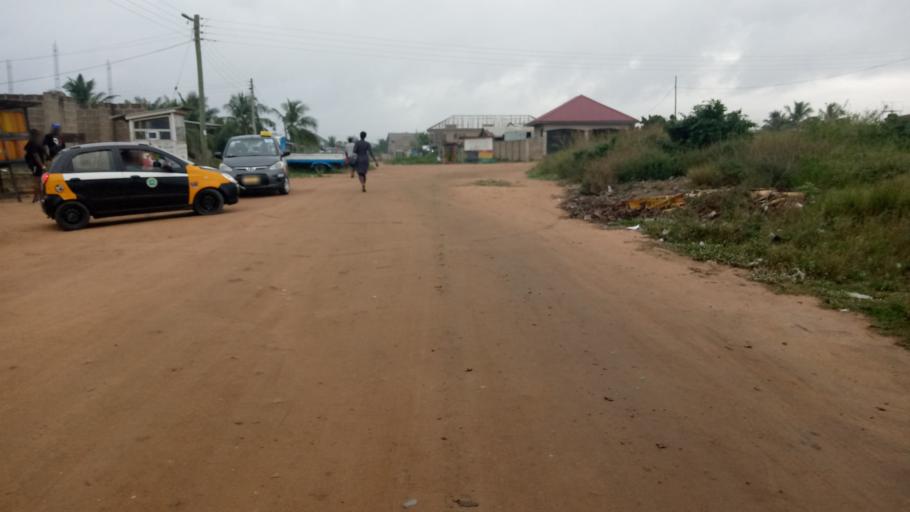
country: GH
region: Central
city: Kasoa
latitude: 5.4992
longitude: -0.4099
